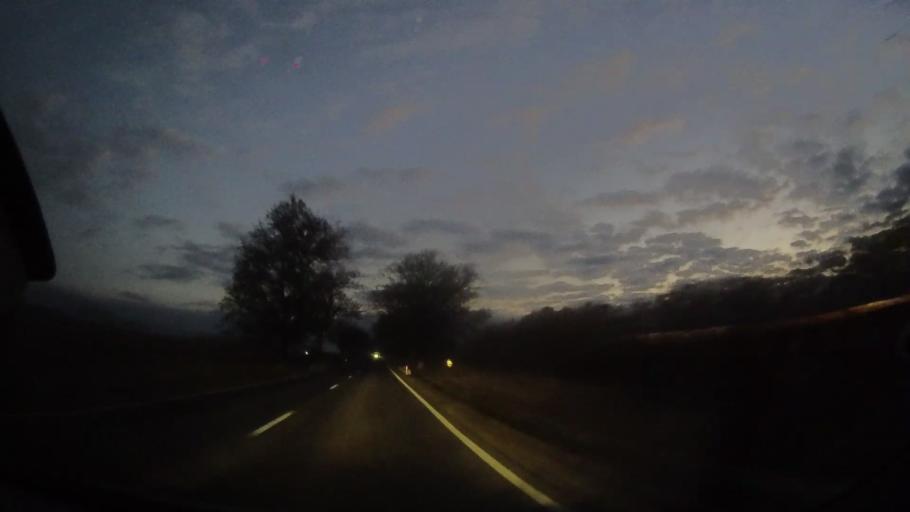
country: RO
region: Tulcea
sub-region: Comuna Mihail Kogalniceanu
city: Mihail Kogalniceanu
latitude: 45.0598
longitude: 28.7375
